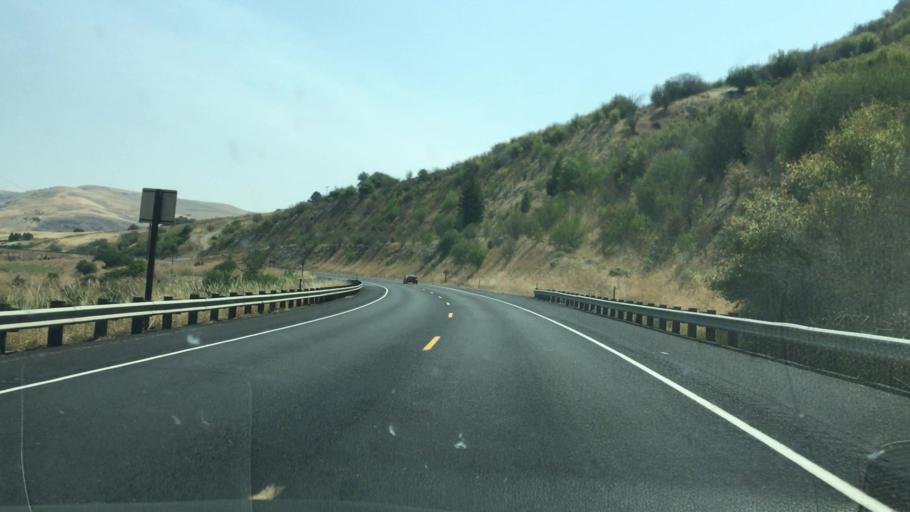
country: US
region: Idaho
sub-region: Nez Perce County
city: Lapwai
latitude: 46.4416
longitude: -116.8404
